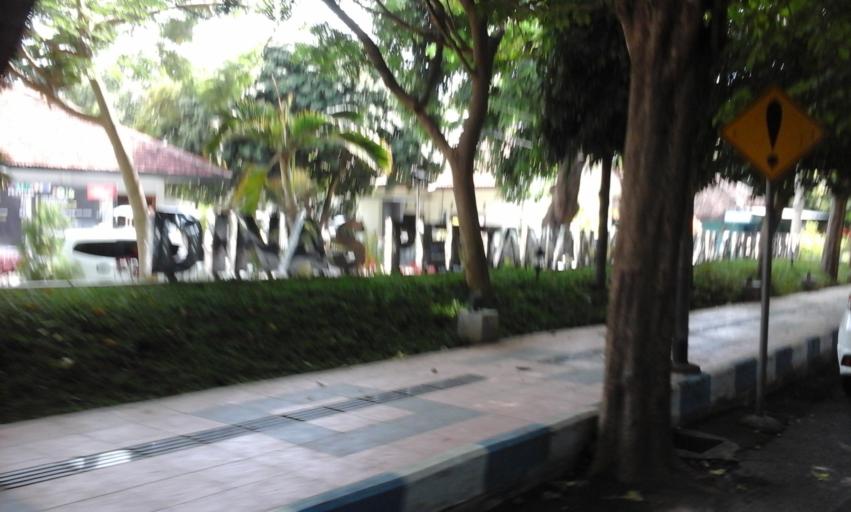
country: ID
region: East Java
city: Cungking
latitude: -8.2165
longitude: 114.3600
